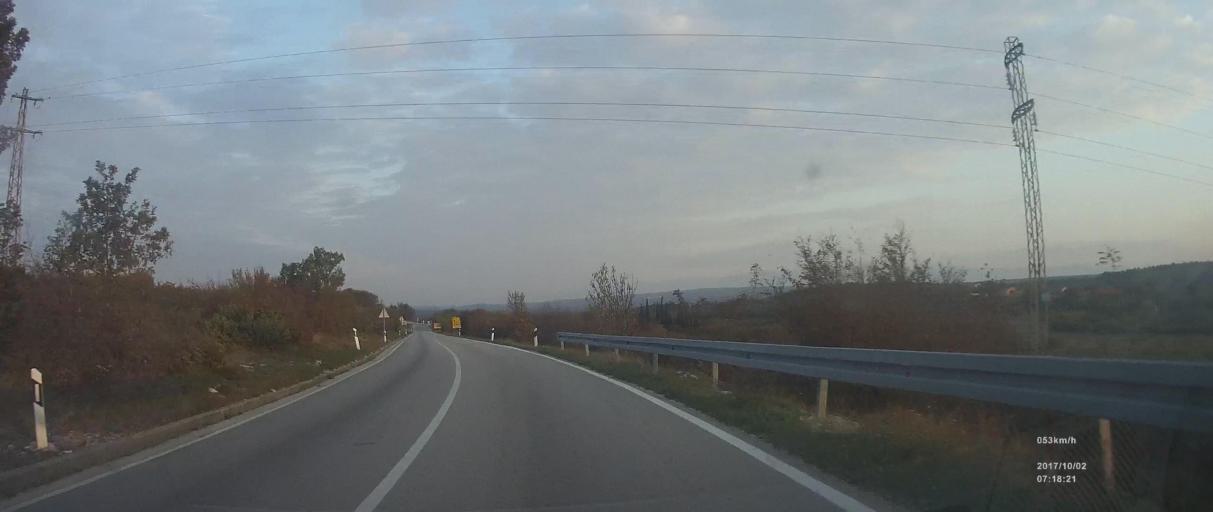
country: HR
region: Zadarska
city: Benkovac
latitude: 44.0171
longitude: 15.5949
